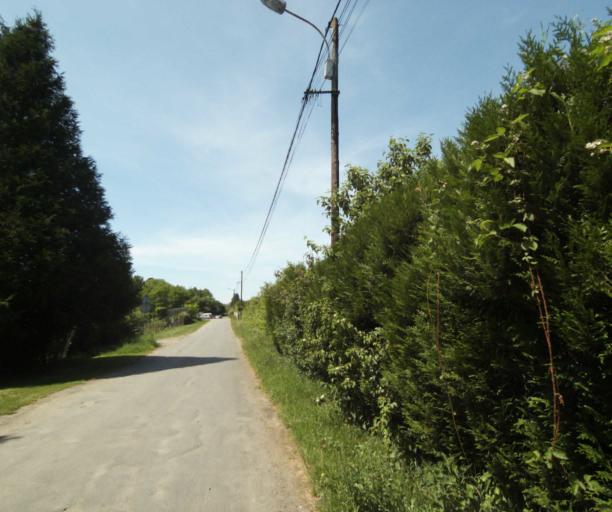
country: FR
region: Champagne-Ardenne
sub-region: Departement des Ardennes
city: Charleville-Mezieres
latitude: 49.7728
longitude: 4.7017
